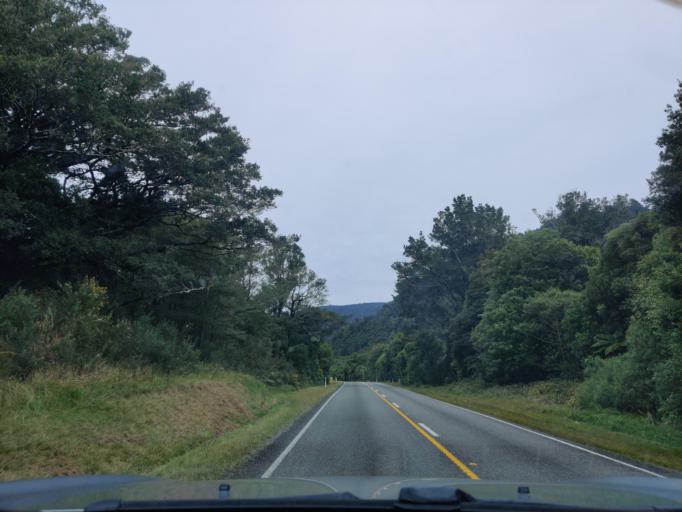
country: NZ
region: West Coast
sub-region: Buller District
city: Westport
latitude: -41.8304
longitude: 171.6487
